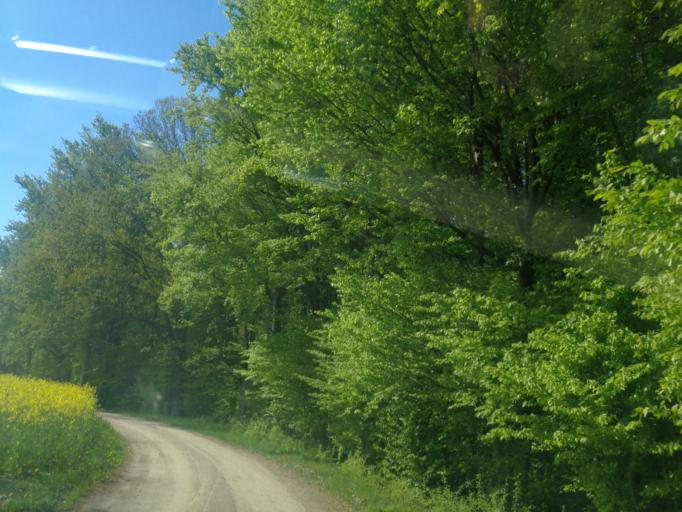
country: PL
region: Warmian-Masurian Voivodeship
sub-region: Powiat ilawski
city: Zalewo
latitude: 53.7594
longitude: 19.6790
